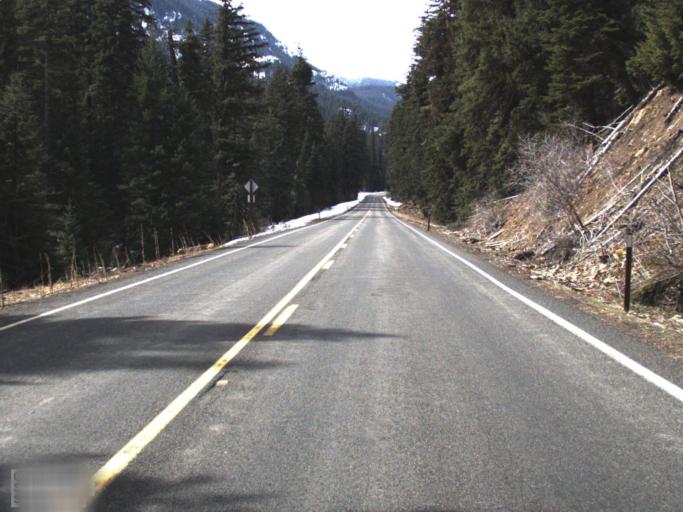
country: US
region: Washington
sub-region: Kittitas County
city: Cle Elum
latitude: 46.9771
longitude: -121.1808
